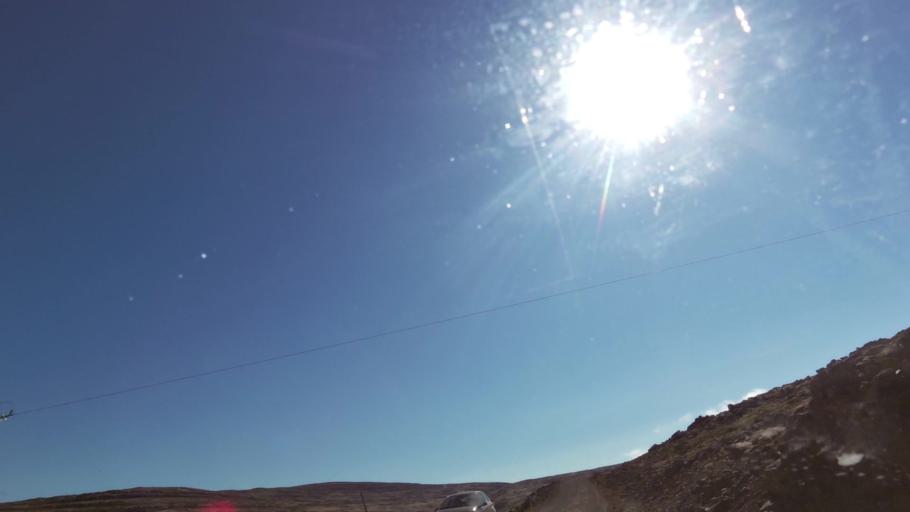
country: IS
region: West
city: Olafsvik
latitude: 65.5515
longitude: -24.2033
